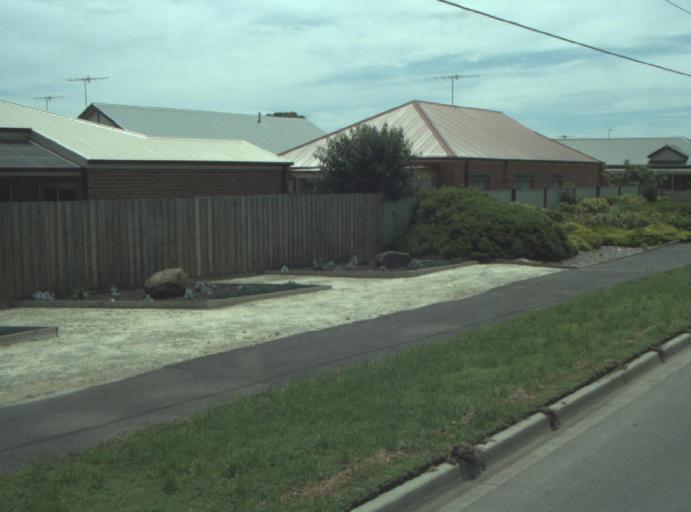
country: AU
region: Victoria
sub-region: Greater Geelong
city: Lara
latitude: -38.0283
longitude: 144.3954
